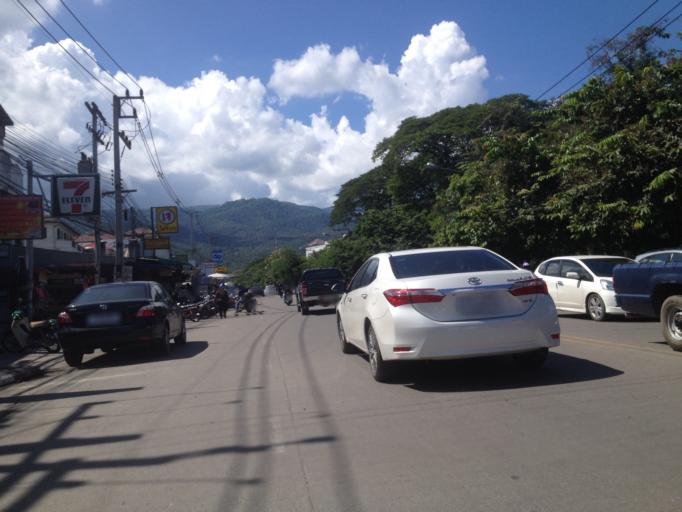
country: TH
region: Chiang Mai
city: Chiang Mai
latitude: 18.7917
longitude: 98.9585
